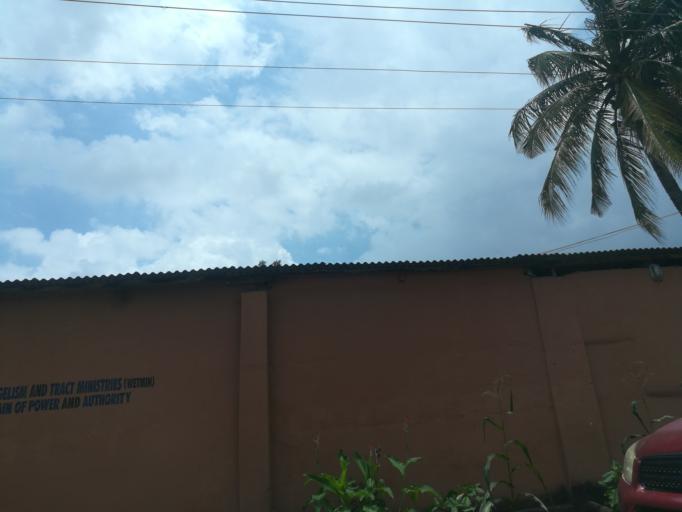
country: NG
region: Lagos
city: Somolu
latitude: 6.5503
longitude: 3.3609
